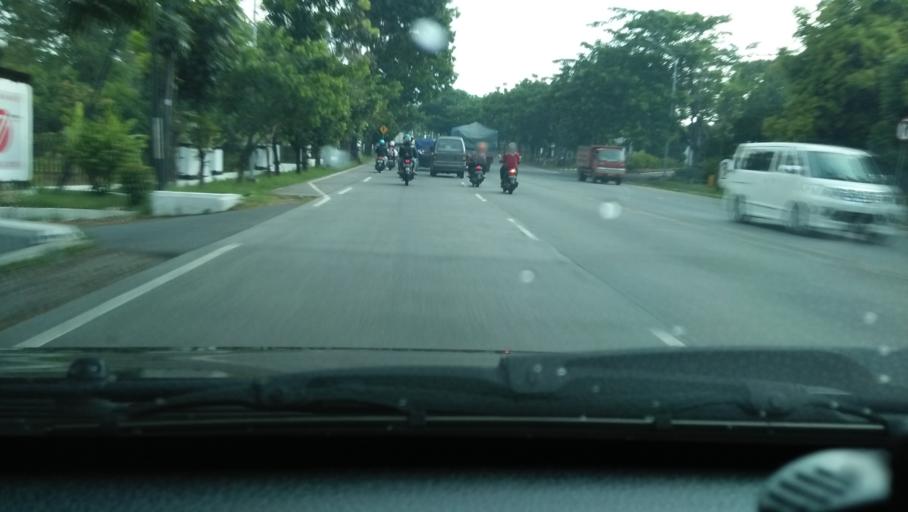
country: ID
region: Central Java
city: Ungaran
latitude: -7.0844
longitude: 110.4099
